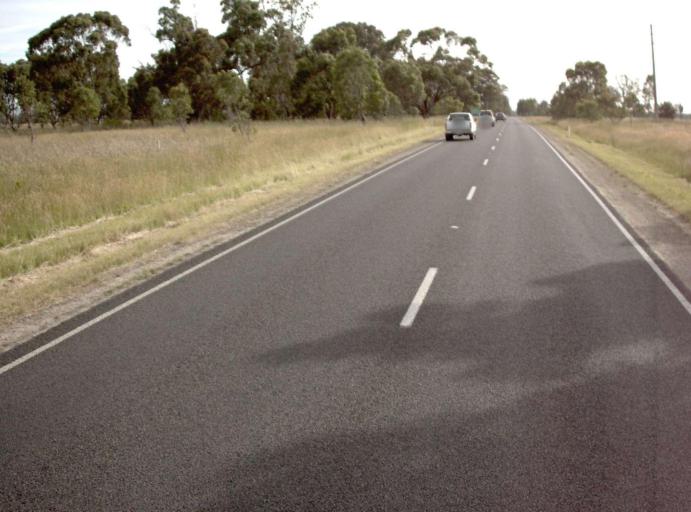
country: AU
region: Victoria
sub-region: Latrobe
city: Traralgon
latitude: -38.1163
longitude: 146.5791
